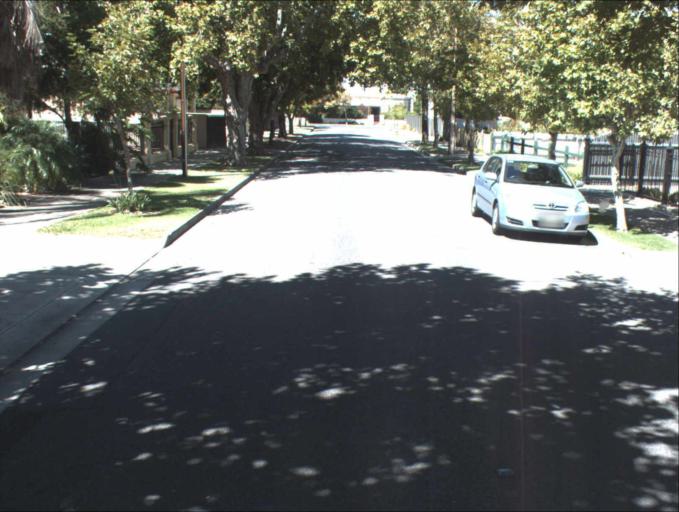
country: AU
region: South Australia
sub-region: Port Adelaide Enfield
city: Birkenhead
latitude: -34.8341
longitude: 138.4866
